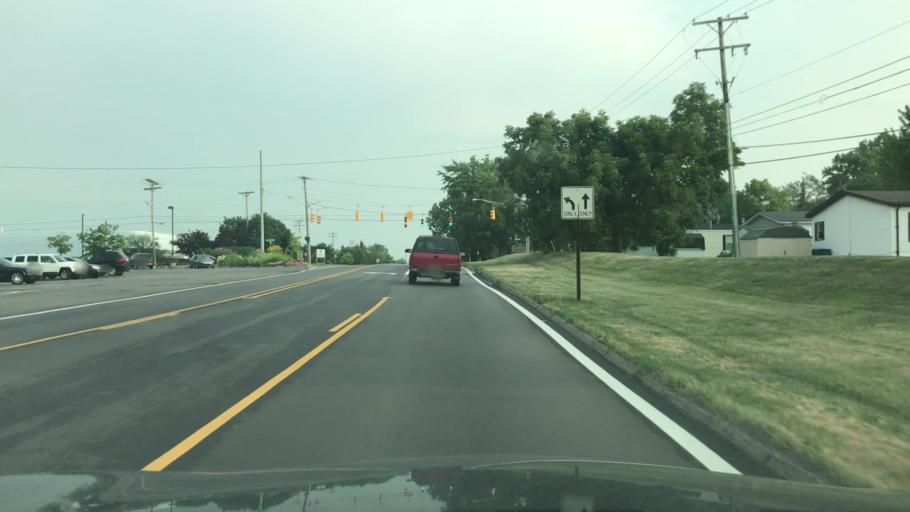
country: US
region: Michigan
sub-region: Oakland County
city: Novi
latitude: 42.4907
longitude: -83.4361
